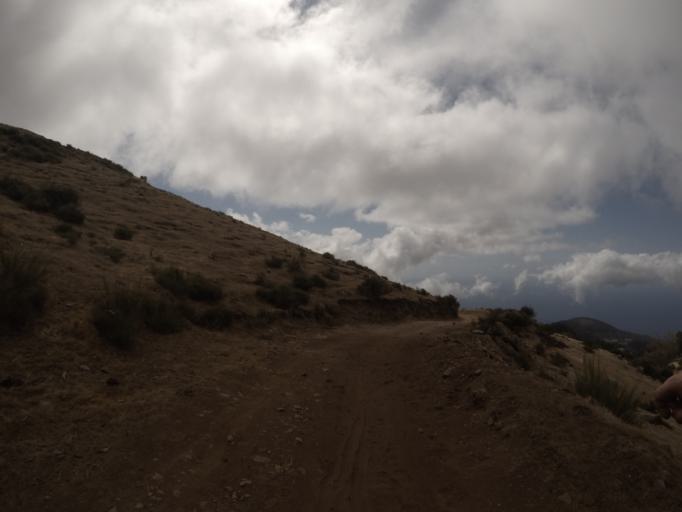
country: PT
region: Madeira
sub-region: Camara de Lobos
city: Curral das Freiras
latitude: 32.7150
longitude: -17.0093
